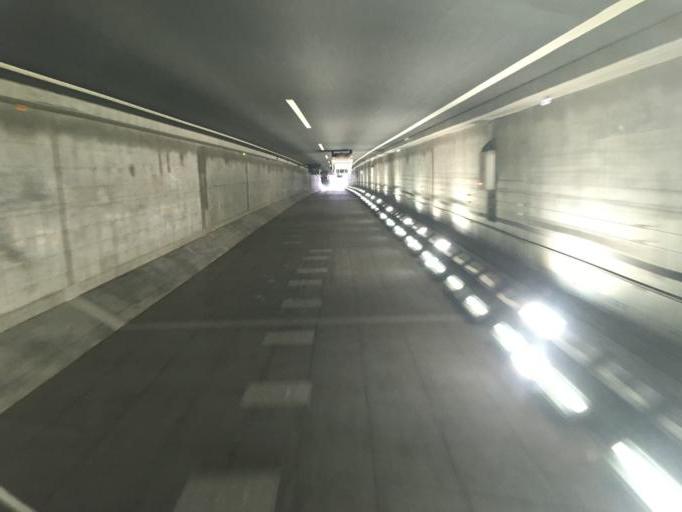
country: JP
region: Kanagawa
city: Zama
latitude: 35.5162
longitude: 139.3595
